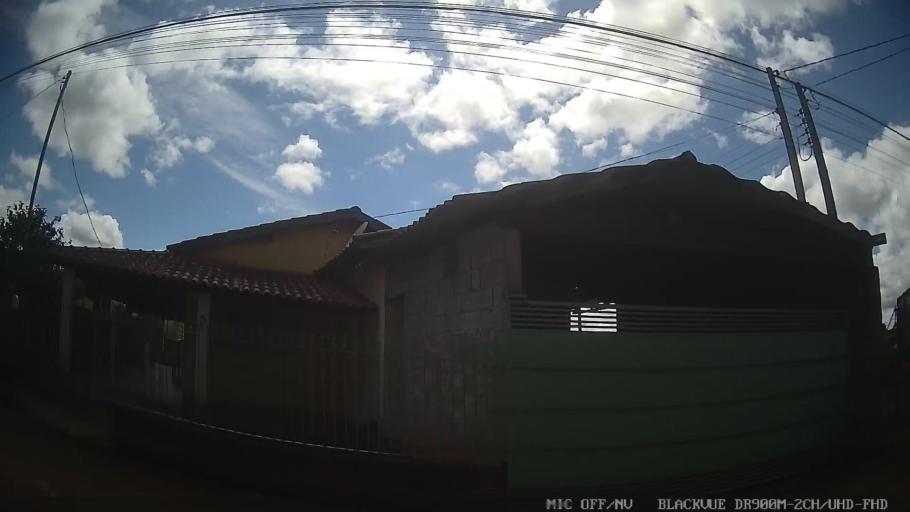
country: BR
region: Sao Paulo
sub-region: Amparo
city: Amparo
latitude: -22.8565
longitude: -46.7162
